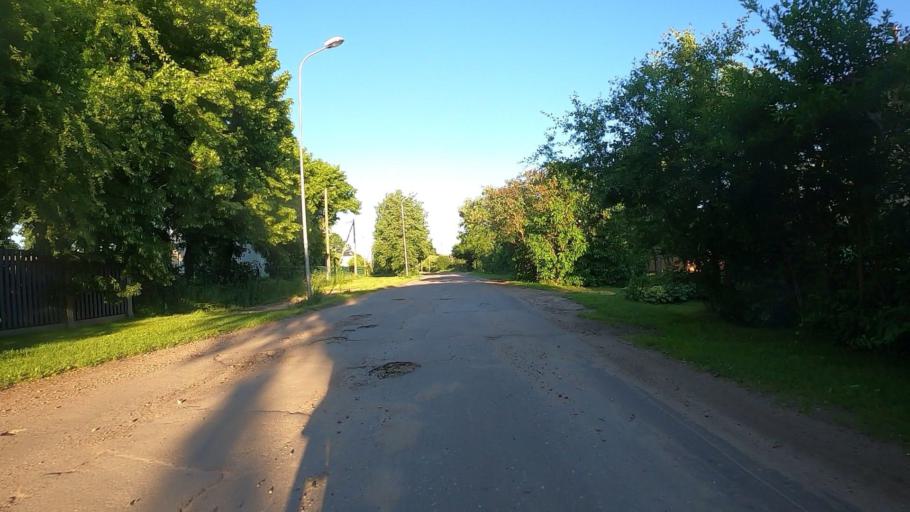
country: LV
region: Kekava
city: Kekava
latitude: 56.8638
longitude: 24.2625
